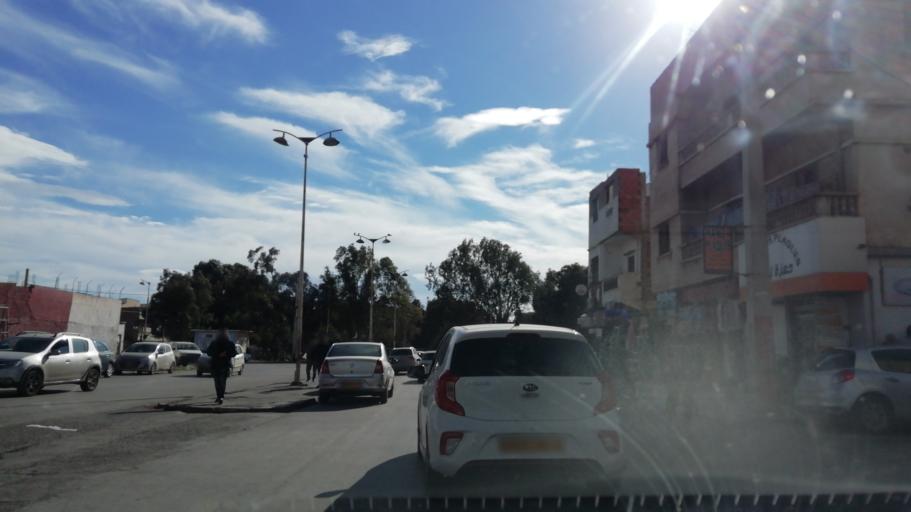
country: DZ
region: Oran
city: Oran
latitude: 35.6974
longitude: -0.6189
